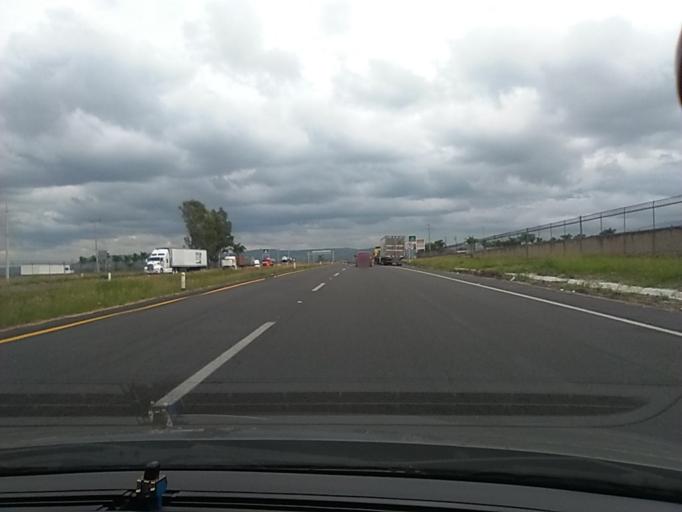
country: MX
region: Jalisco
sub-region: Tonala
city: Mismaloya (Fraccionamiento Pedregal de Santa Martha)
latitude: 20.6054
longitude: -103.1309
